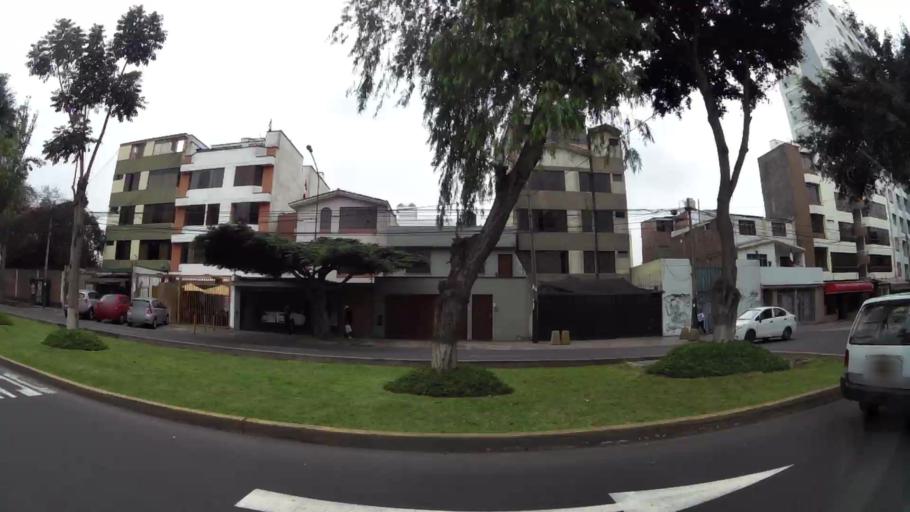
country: PE
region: Lima
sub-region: Lima
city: Surco
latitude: -12.1153
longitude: -77.0071
